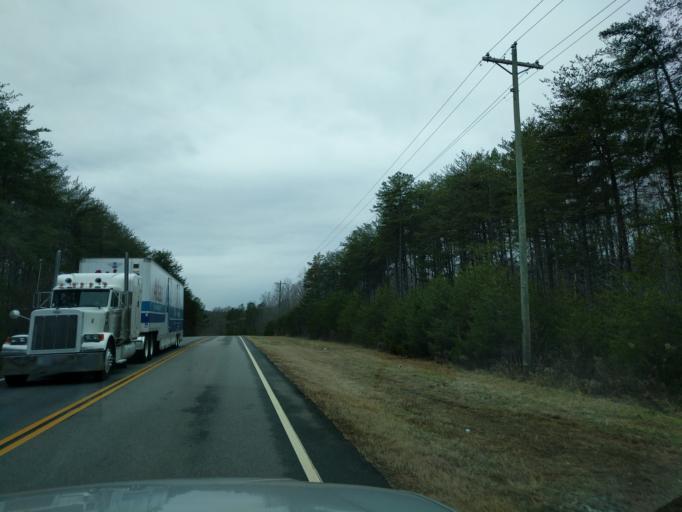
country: US
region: South Carolina
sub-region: Greenville County
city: Slater-Marietta
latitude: 35.0791
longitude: -82.5042
